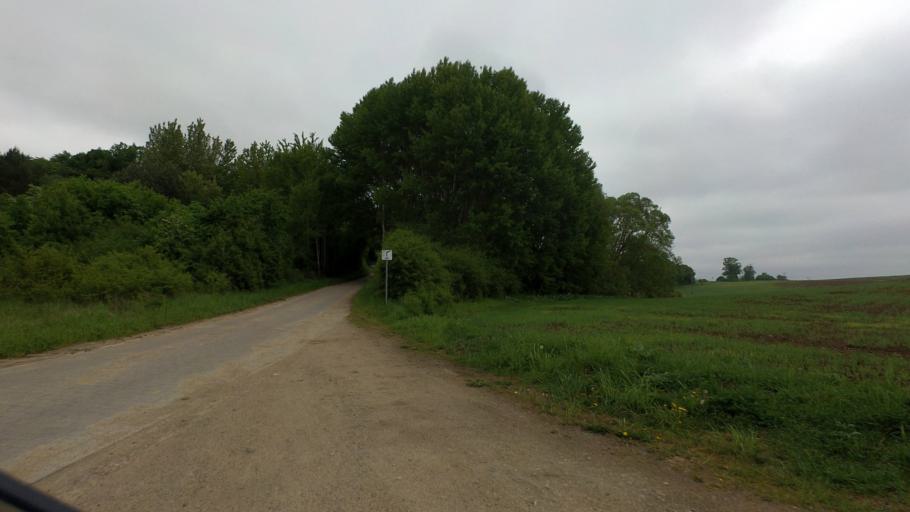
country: DE
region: Mecklenburg-Vorpommern
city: Wustrow
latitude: 53.4519
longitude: 13.1846
